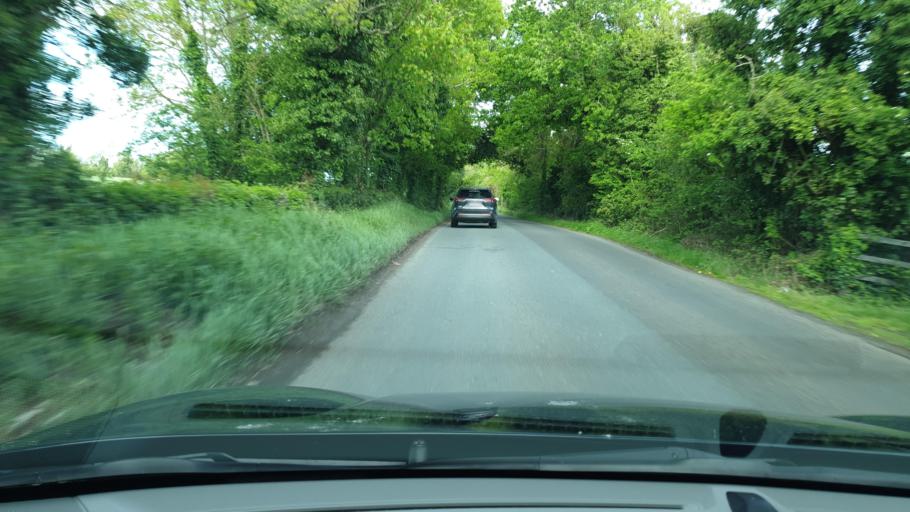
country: IE
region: Leinster
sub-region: An Mhi
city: Ashbourne
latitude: 53.5358
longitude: -6.3876
